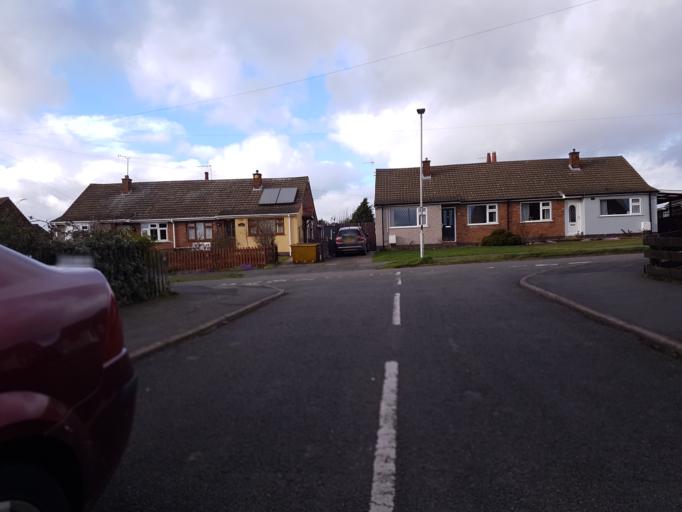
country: GB
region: England
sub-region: Leicestershire
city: Earl Shilton
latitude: 52.5689
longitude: -1.3234
